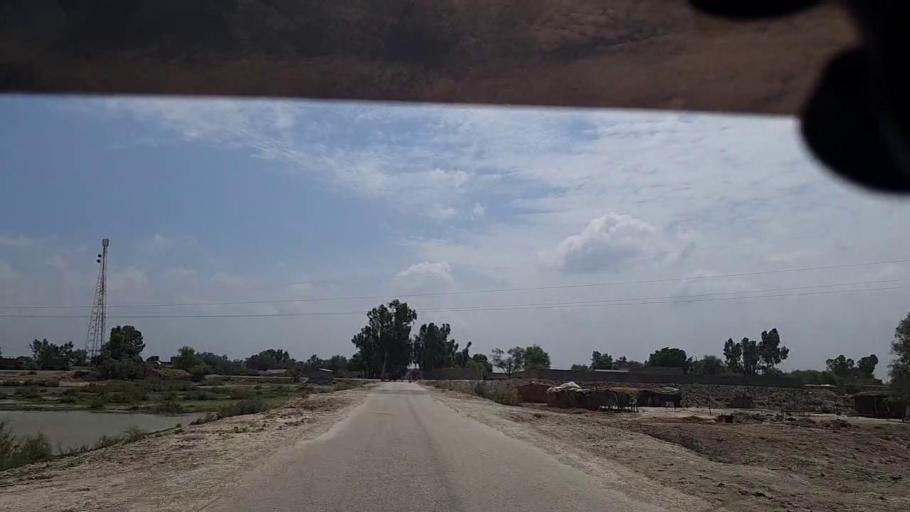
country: PK
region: Sindh
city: Ghauspur
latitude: 28.0895
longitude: 68.9622
